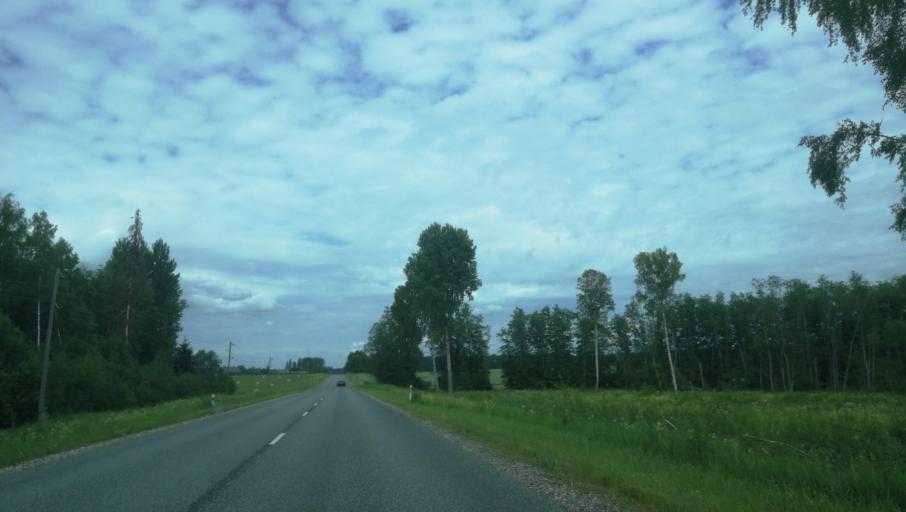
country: LV
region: Naukseni
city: Naukseni
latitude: 57.7505
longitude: 25.4326
